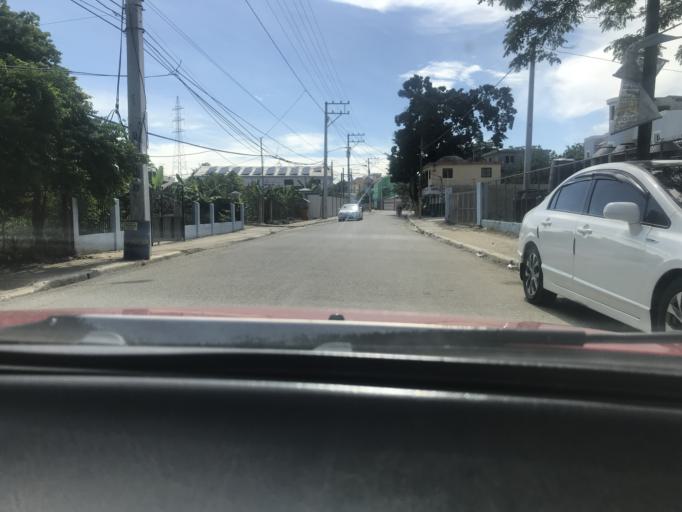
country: DO
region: Santiago
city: Licey al Medio
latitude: 19.4060
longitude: -70.6301
